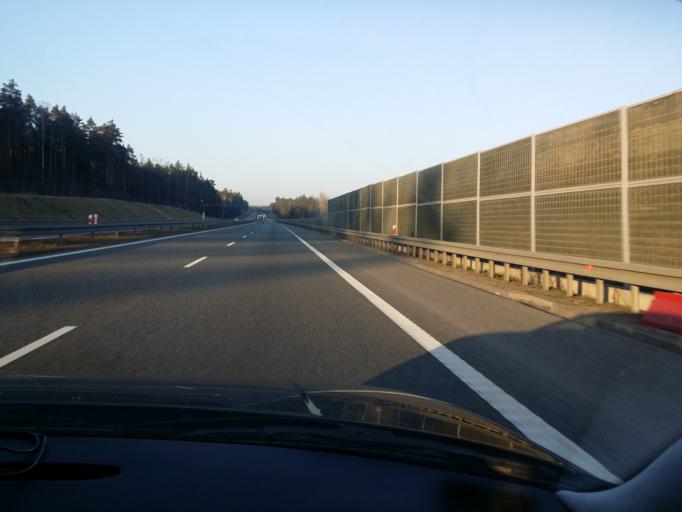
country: PL
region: Swietokrzyskie
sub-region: Powiat skarzyski
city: Suchedniow
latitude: 51.0579
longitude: 20.8283
